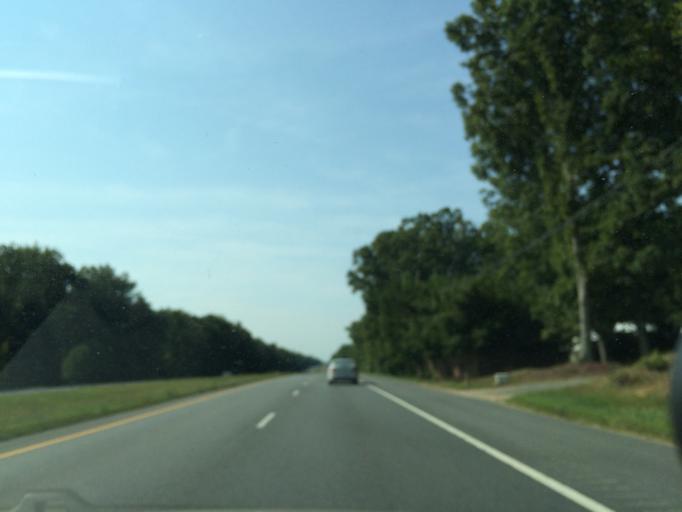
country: US
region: Maryland
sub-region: Charles County
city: La Plata
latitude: 38.4950
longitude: -76.9871
